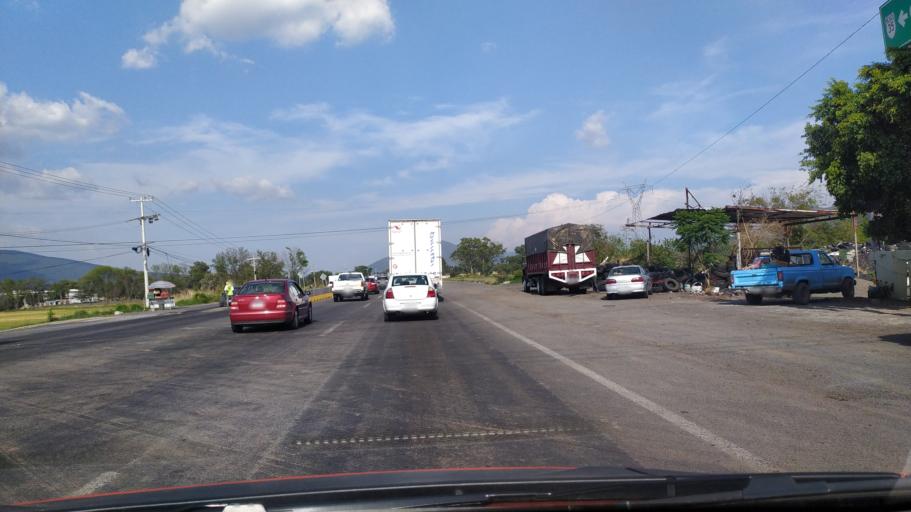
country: MX
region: Jalisco
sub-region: Ixtlahuacan de los Membrillos
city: Valle de los Girasoles [Fraccionamiento]
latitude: 20.4047
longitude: -103.1830
